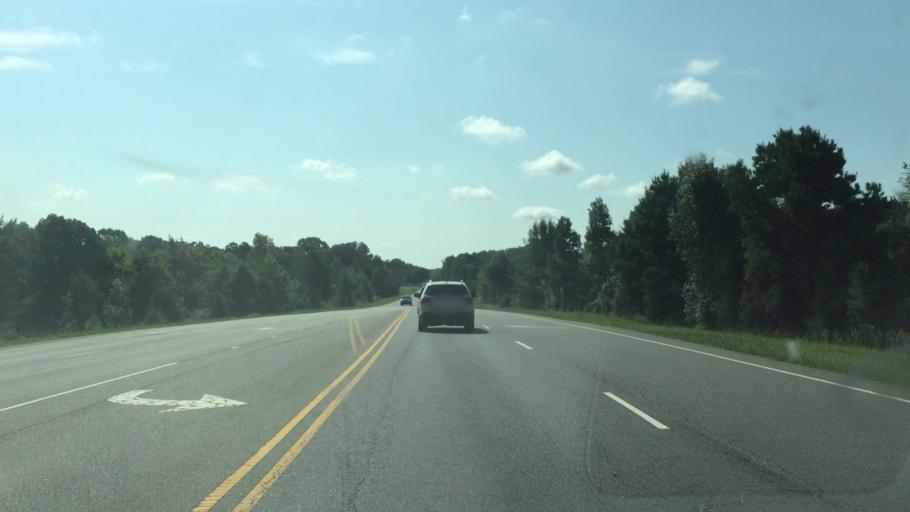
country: US
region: North Carolina
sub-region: Mecklenburg County
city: Mint Hill
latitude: 35.1768
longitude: -80.6256
